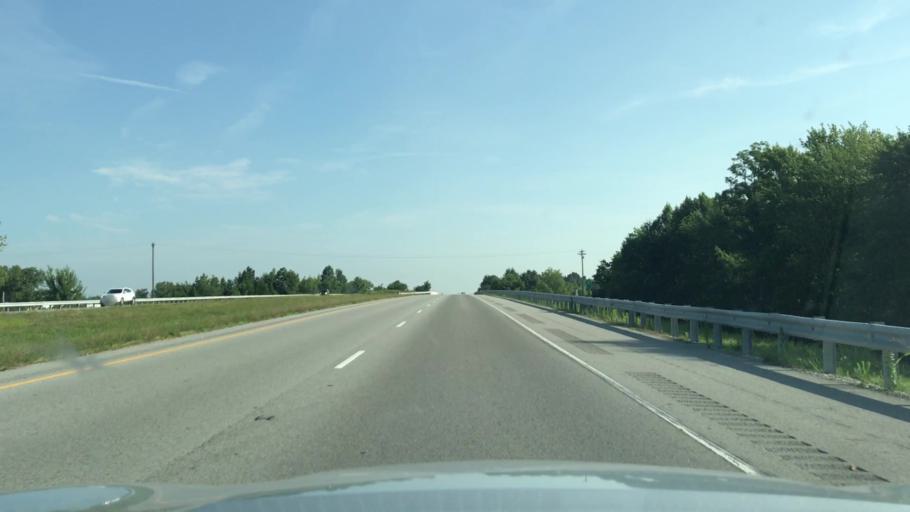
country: US
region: Tennessee
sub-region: Putnam County
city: Algood
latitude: 36.1879
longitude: -85.4619
